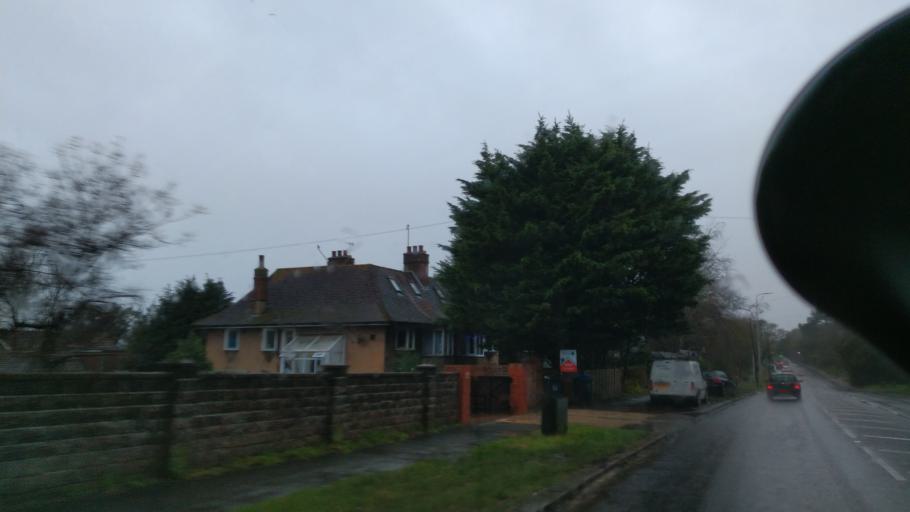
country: GB
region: England
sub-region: West Sussex
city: Findon
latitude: 50.8405
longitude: -0.4063
